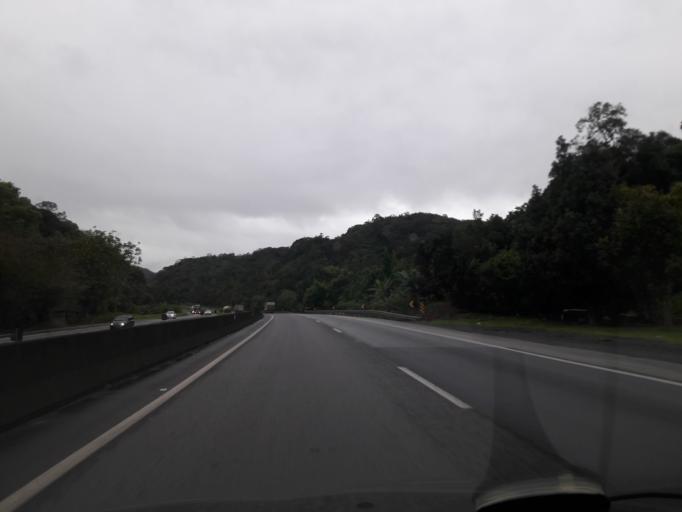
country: BR
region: Sao Paulo
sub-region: Miracatu
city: Miracatu
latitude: -24.2406
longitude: -47.3625
